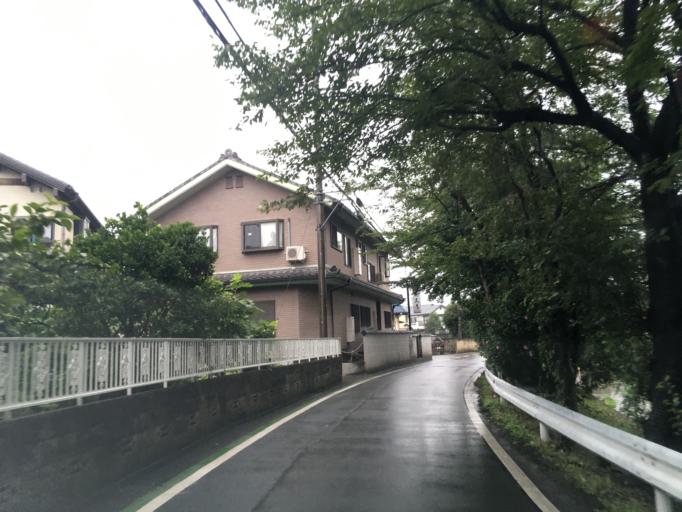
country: JP
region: Saitama
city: Tokorozawa
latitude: 35.7941
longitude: 139.4861
